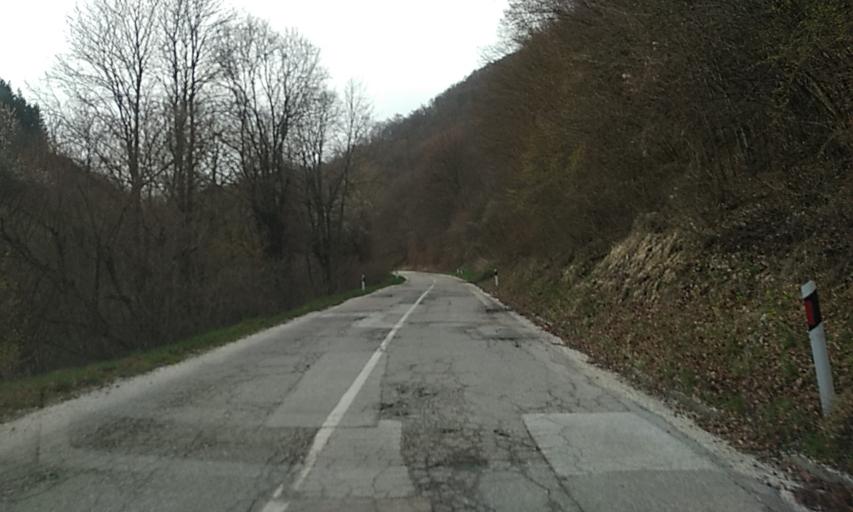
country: RS
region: Central Serbia
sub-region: Pcinjski Okrug
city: Bosilegrad
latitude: 42.5469
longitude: 22.3966
